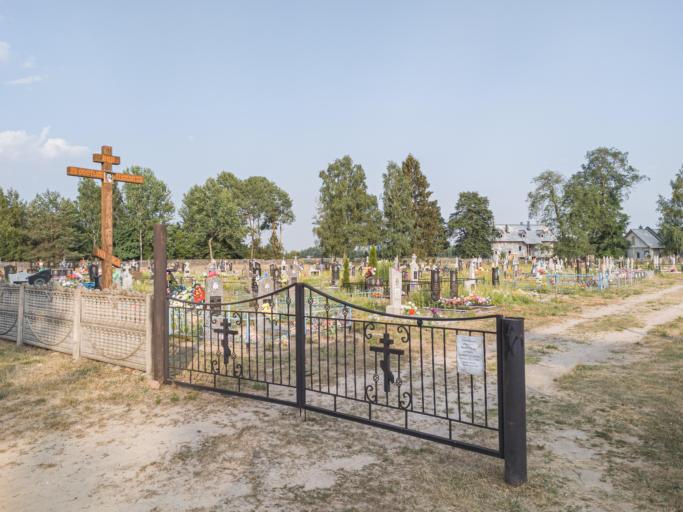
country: BY
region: Brest
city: Zhabinka
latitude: 52.4068
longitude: 24.0925
